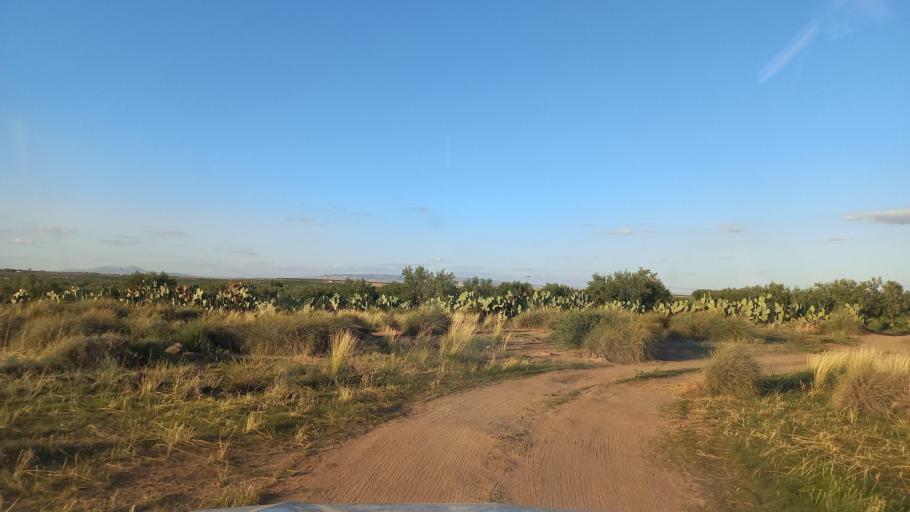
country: TN
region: Al Qasrayn
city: Sbiba
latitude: 35.4207
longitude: 9.1308
